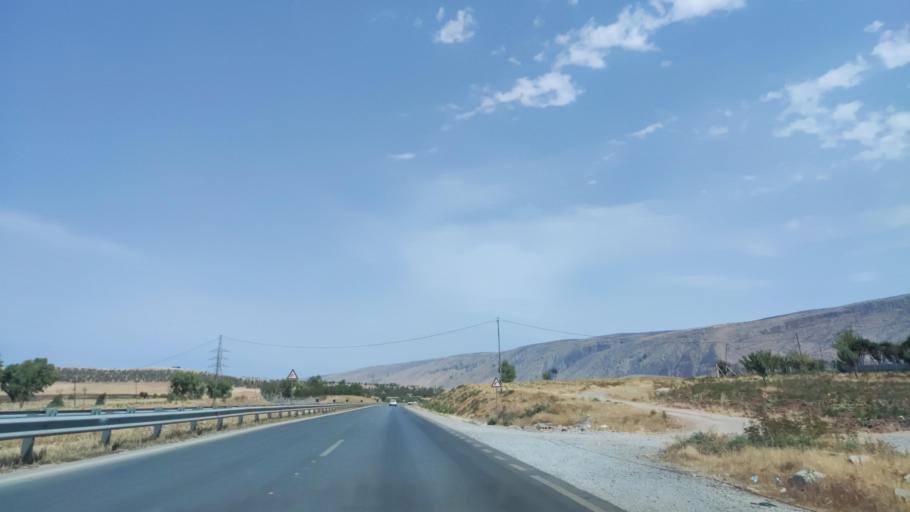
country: IQ
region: Arbil
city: Shaqlawah
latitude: 36.4746
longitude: 44.3811
